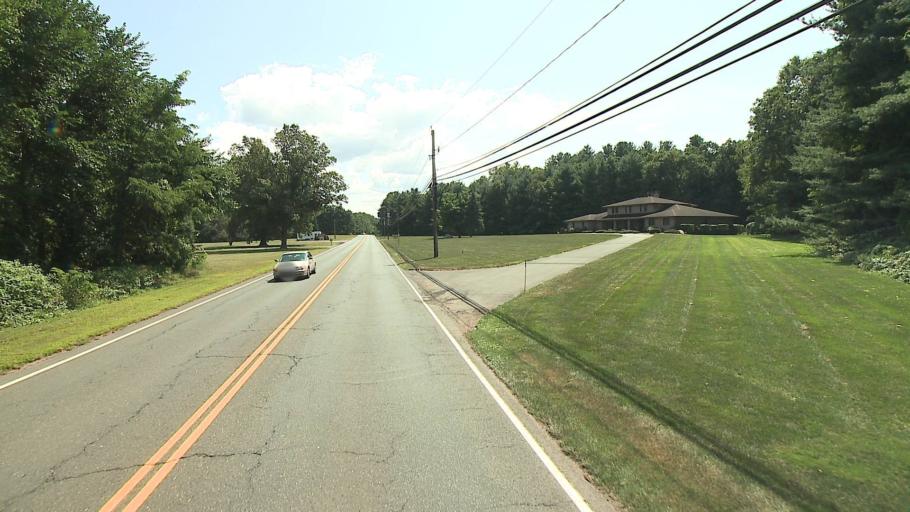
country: US
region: Connecticut
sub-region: Hartford County
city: Broad Brook
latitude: 41.9317
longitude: -72.5567
